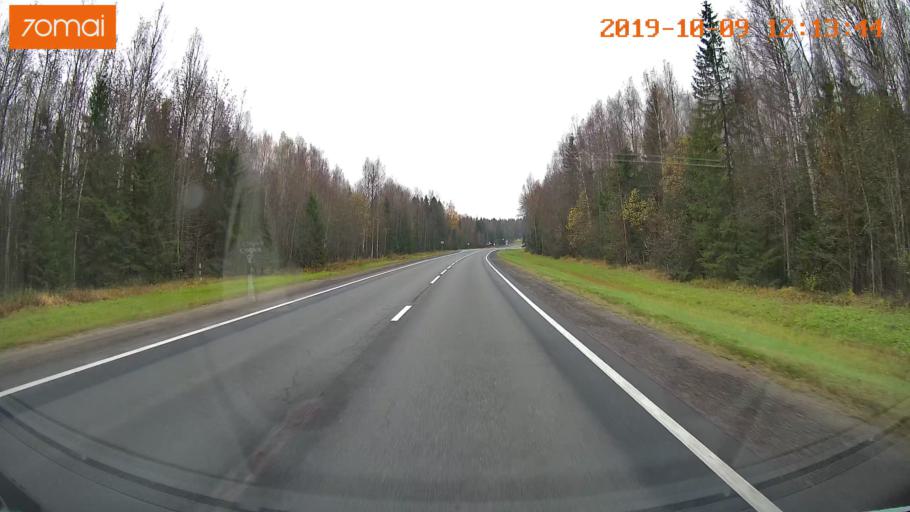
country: RU
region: Jaroslavl
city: Prechistoye
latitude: 58.5060
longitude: 40.3441
